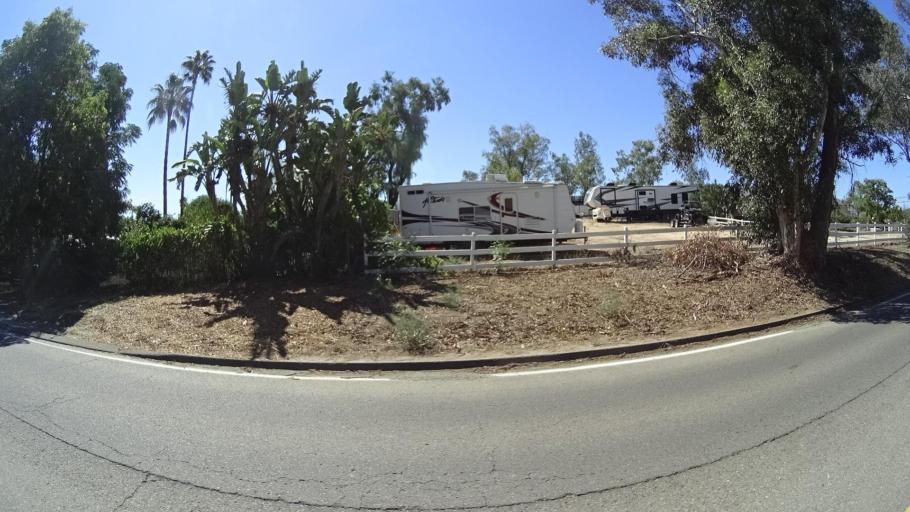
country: US
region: California
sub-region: San Diego County
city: Ramona
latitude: 33.0403
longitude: -116.8479
